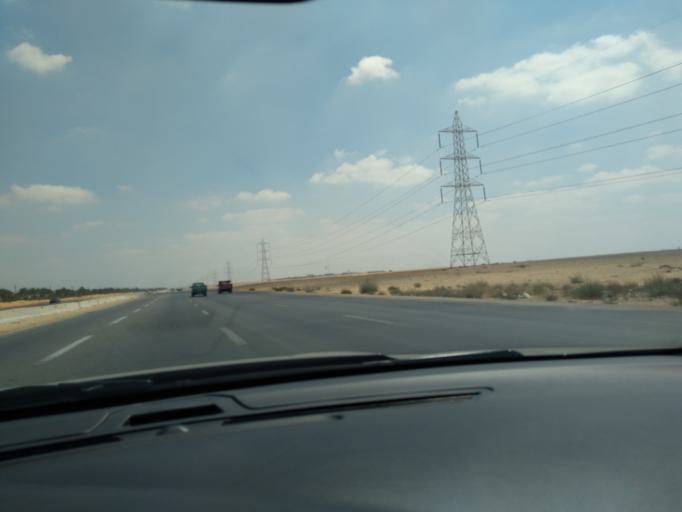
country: EG
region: Al Isma'iliyah
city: At Tall al Kabir
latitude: 30.3814
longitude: 31.9471
